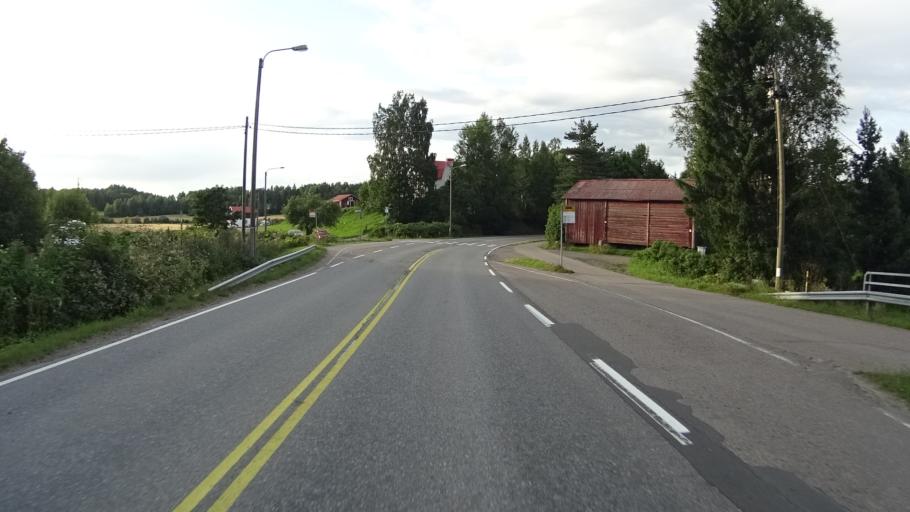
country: FI
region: Uusimaa
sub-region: Helsinki
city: Nurmijaervi
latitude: 60.3422
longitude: 24.8652
